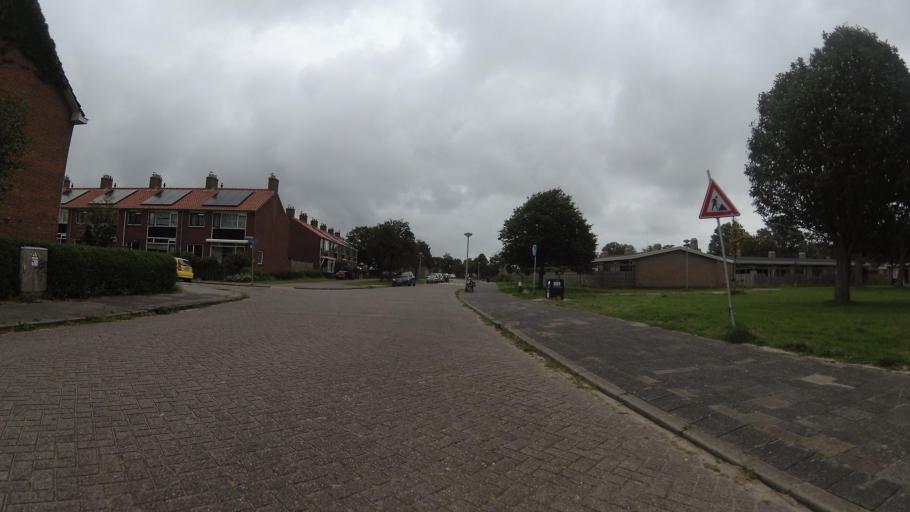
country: NL
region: North Holland
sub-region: Gemeente Den Helder
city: Den Helder
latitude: 52.9383
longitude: 4.7461
